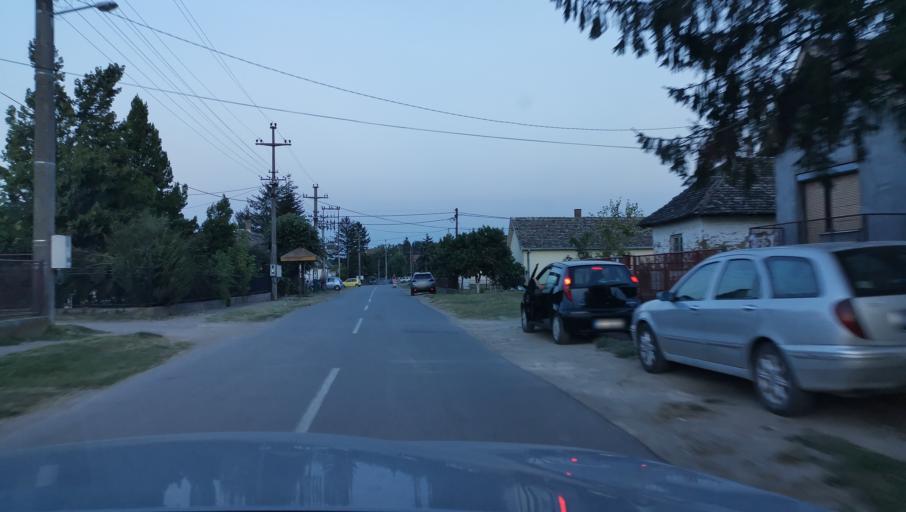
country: RS
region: Central Serbia
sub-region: Belgrade
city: Obrenovac
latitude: 44.6818
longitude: 20.2173
